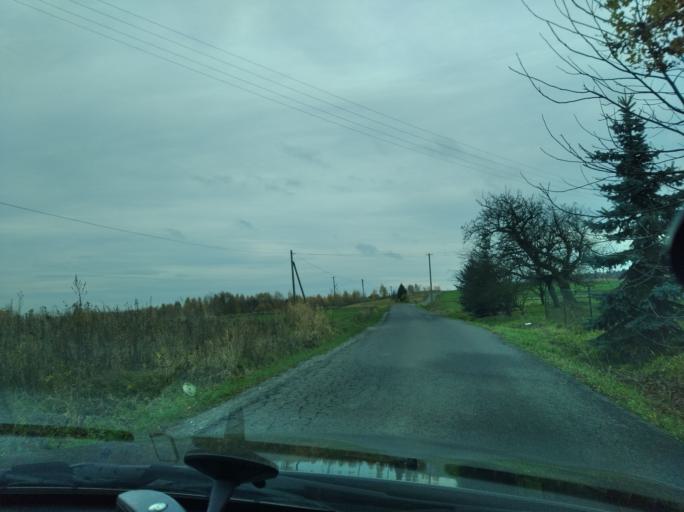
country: PL
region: Subcarpathian Voivodeship
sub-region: Powiat strzyzowski
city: Strzyzow
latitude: 49.9153
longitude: 21.7666
